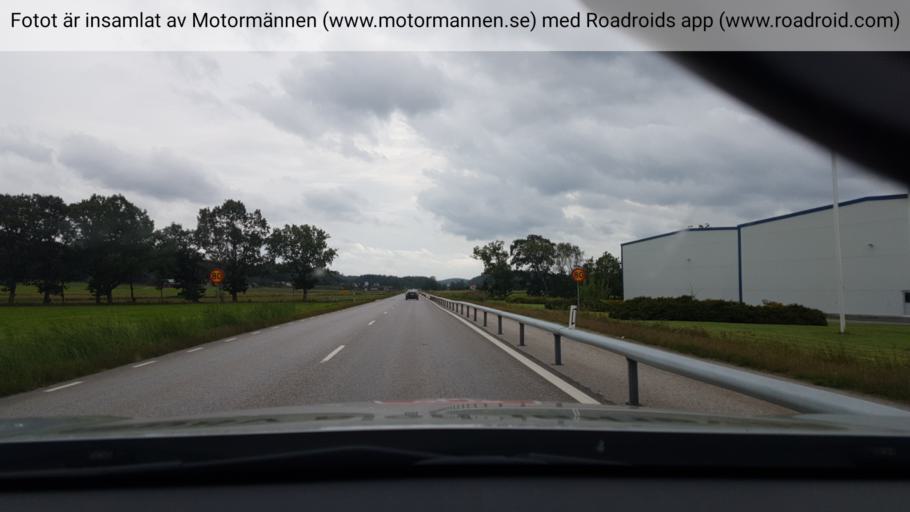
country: SE
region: Vaestra Goetaland
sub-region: Munkedals Kommun
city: Munkedal
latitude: 58.5181
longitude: 11.5753
